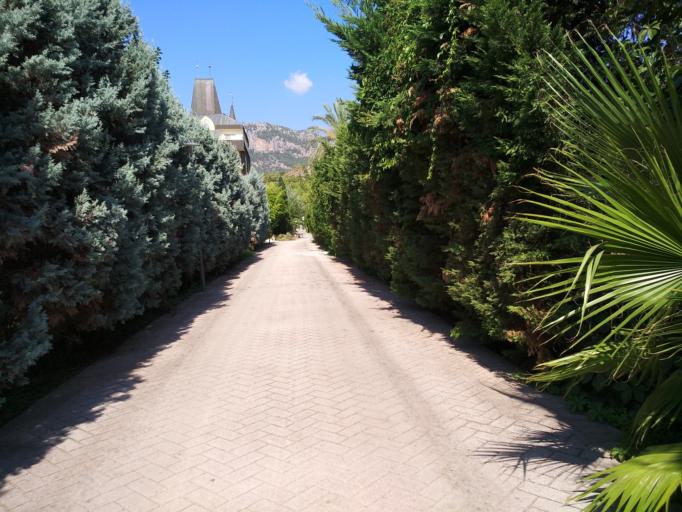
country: TR
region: Antalya
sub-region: Kemer
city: Goeynuek
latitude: 36.6661
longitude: 30.5607
